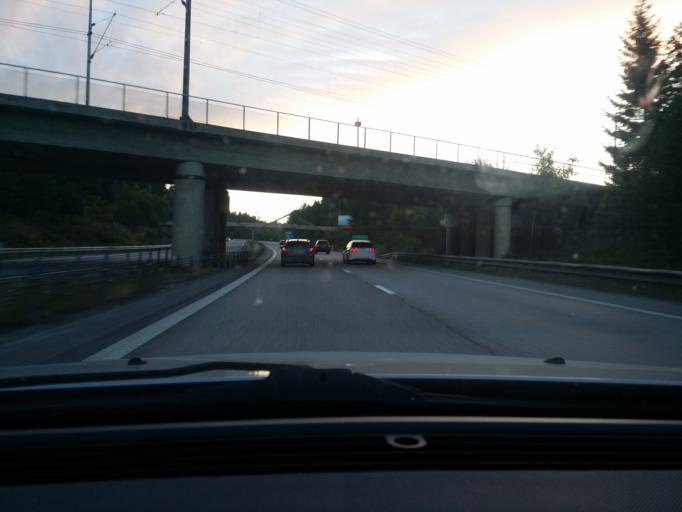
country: SE
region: Uppsala
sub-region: Enkopings Kommun
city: Enkoping
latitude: 59.6484
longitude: 17.0608
